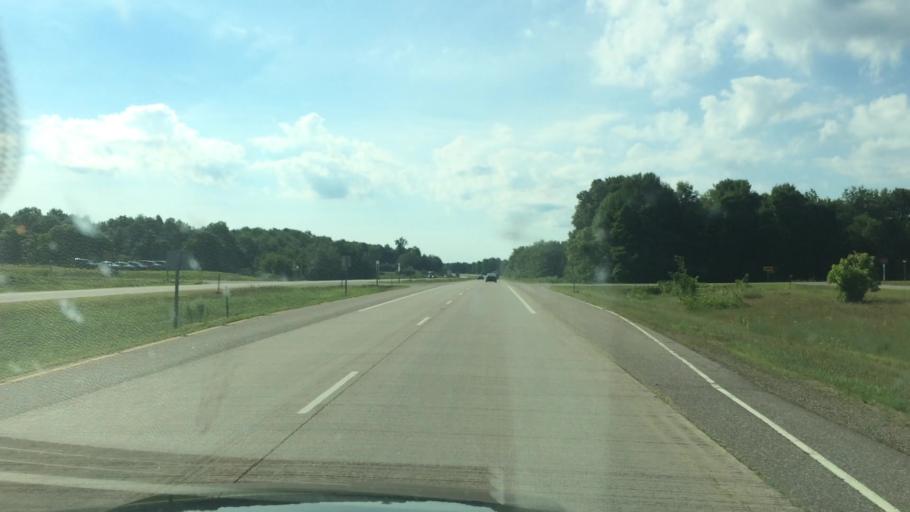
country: US
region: Wisconsin
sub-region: Shawano County
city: Wittenberg
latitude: 44.8111
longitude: -89.0423
